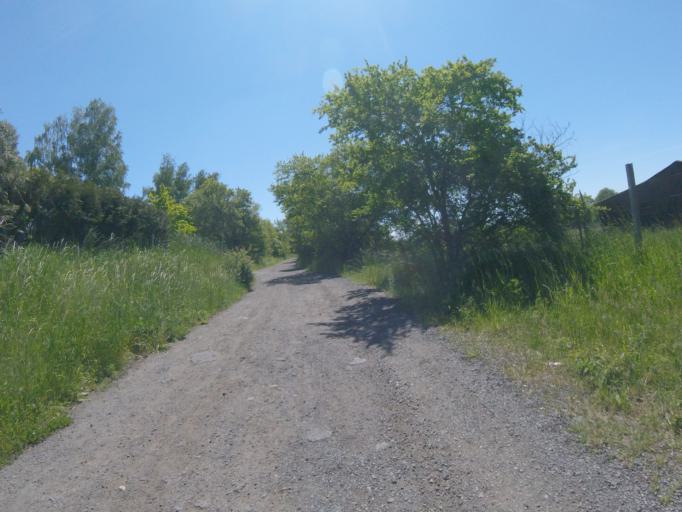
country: DE
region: Brandenburg
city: Teupitz
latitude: 52.1323
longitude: 13.6135
